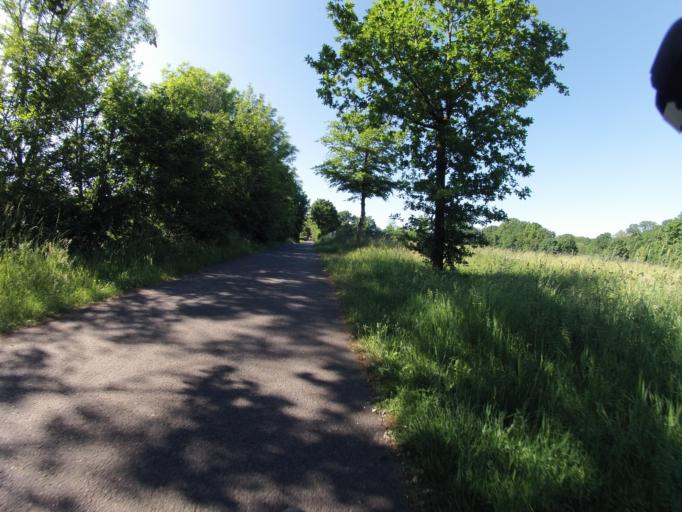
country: DE
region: North Rhine-Westphalia
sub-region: Regierungsbezirk Munster
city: Rheine
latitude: 52.2917
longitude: 7.4322
